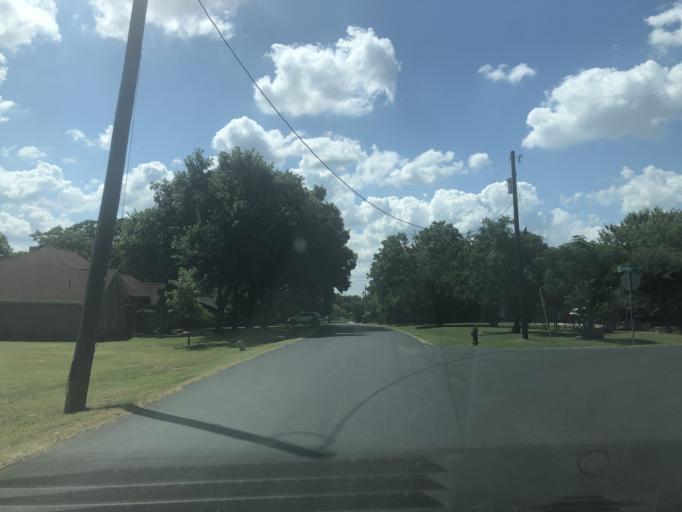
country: US
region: Texas
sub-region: Dallas County
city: Grand Prairie
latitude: 32.7387
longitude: -97.0002
